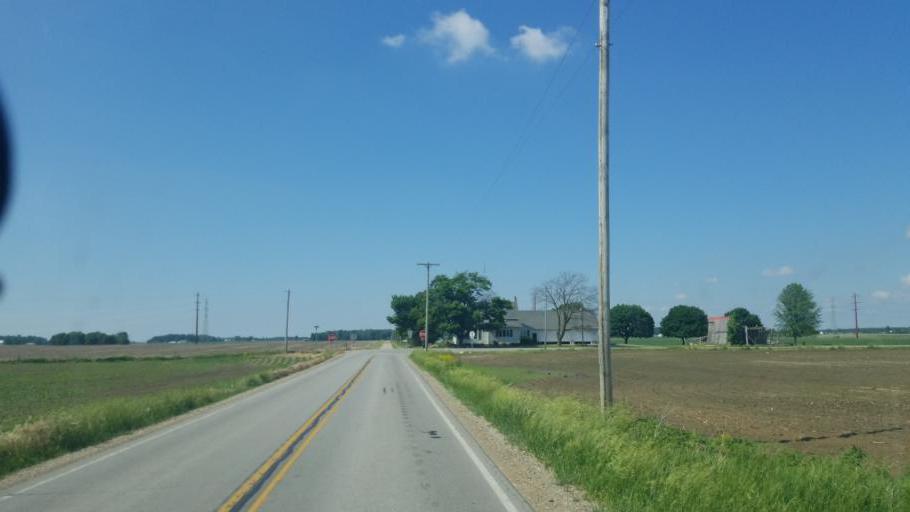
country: US
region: Indiana
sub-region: Marshall County
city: Bourbon
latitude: 41.3135
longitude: -86.0478
